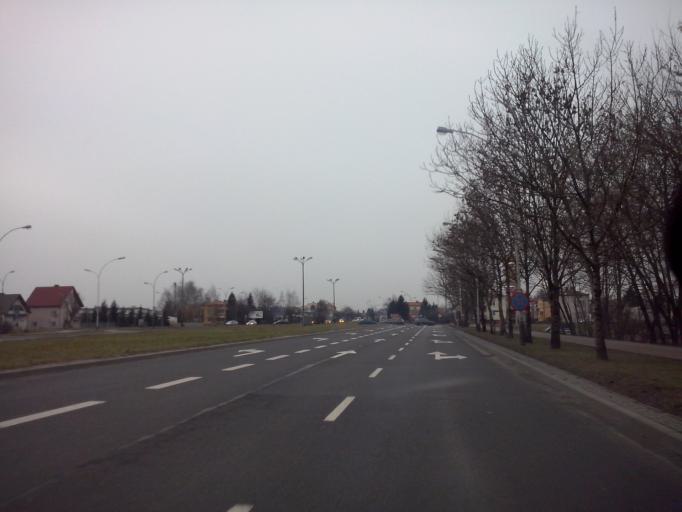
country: PL
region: Lublin Voivodeship
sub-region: Zamosc
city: Zamosc
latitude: 50.7164
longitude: 23.2310
